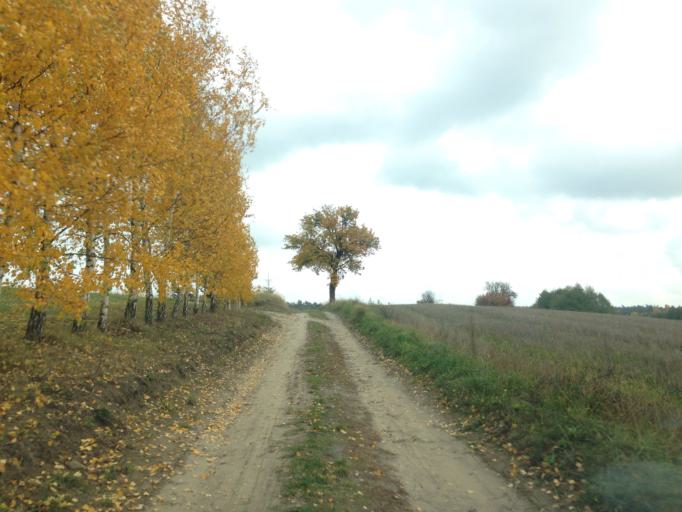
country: PL
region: Kujawsko-Pomorskie
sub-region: Powiat brodnicki
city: Gorzno
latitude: 53.2547
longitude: 19.6815
